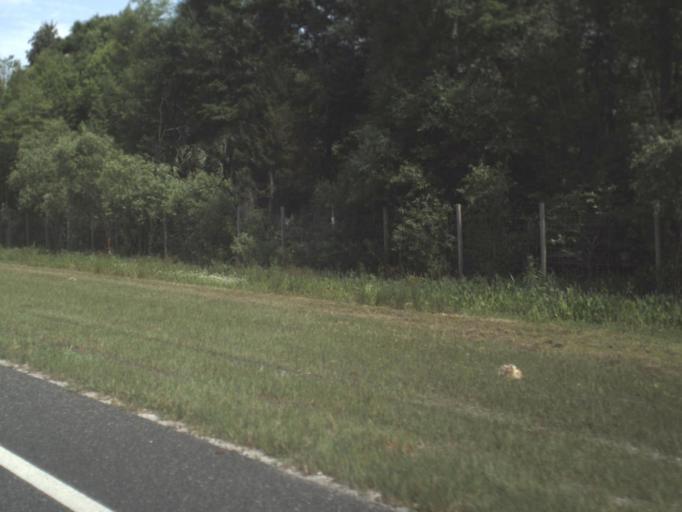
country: US
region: Florida
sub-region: Putnam County
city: Palatka
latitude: 29.6293
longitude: -81.7577
